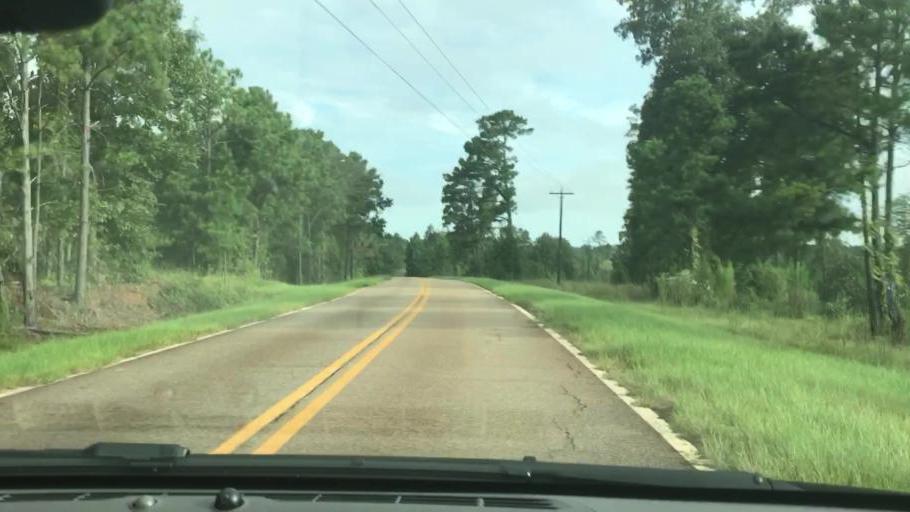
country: US
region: Georgia
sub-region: Stewart County
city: Lumpkin
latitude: 32.0559
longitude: -84.9030
